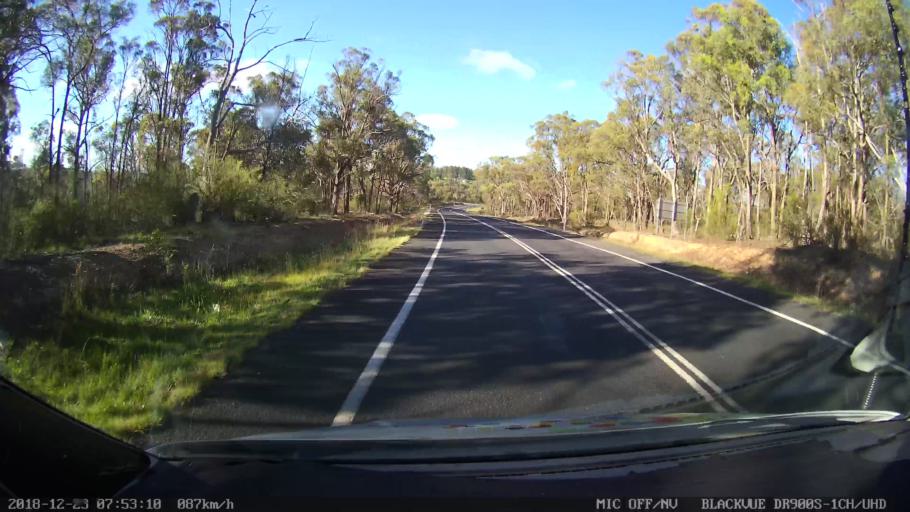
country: AU
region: New South Wales
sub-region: Armidale Dumaresq
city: Armidale
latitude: -30.5346
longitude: 151.8116
